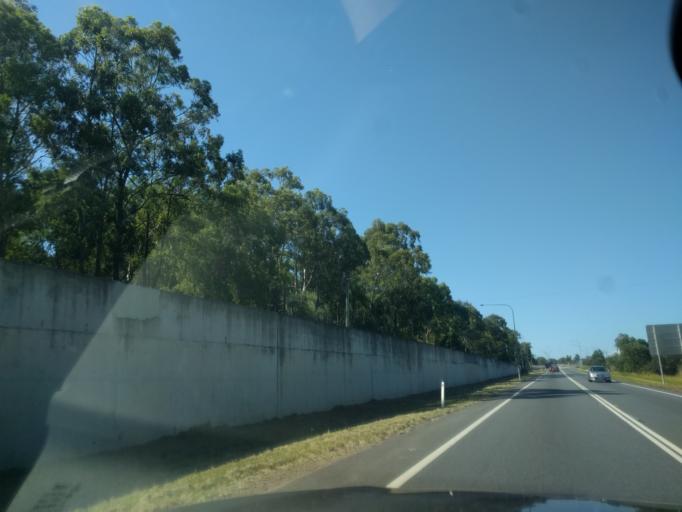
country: AU
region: Queensland
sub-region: Logan
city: Park Ridge South
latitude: -27.7207
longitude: 153.0315
